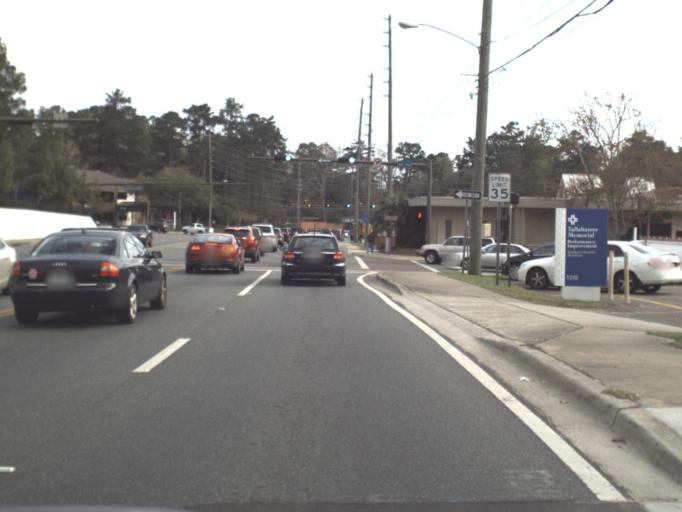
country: US
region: Florida
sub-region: Leon County
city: Tallahassee
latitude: 30.4568
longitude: -84.2629
